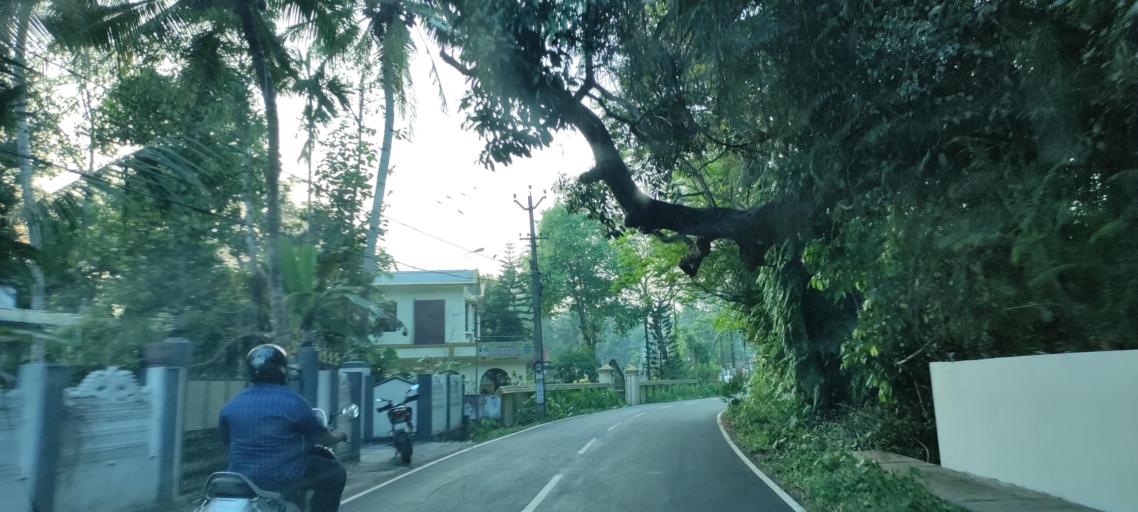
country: IN
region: Kerala
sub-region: Alappuzha
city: Mavelikara
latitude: 9.2679
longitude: 76.5438
